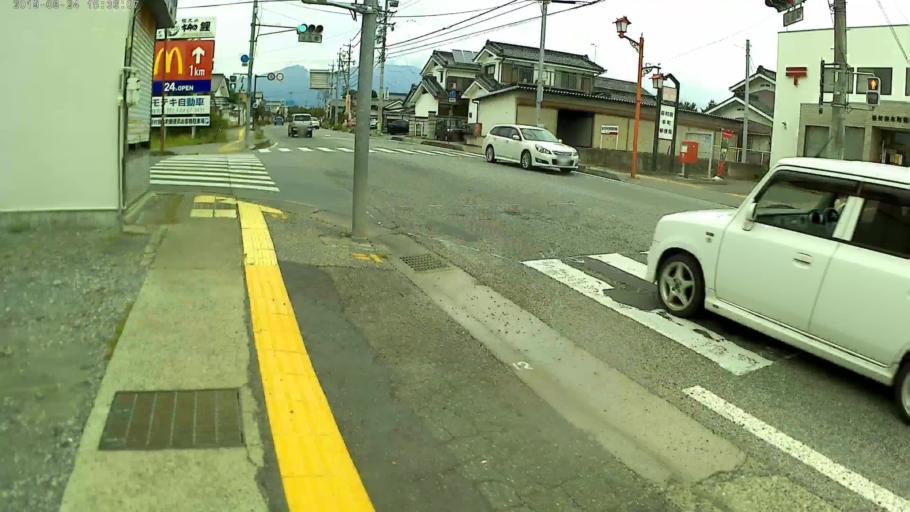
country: JP
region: Nagano
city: Saku
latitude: 36.2760
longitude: 138.4782
